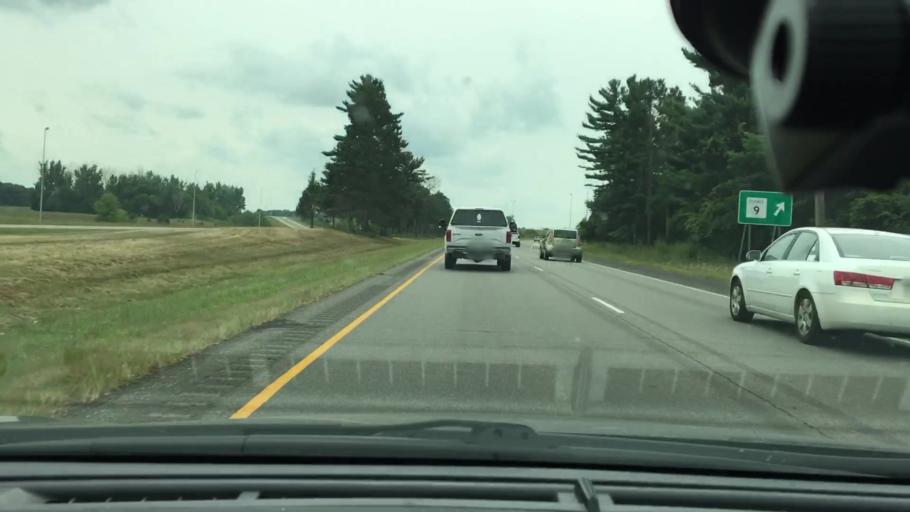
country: US
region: Minnesota
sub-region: Mille Lacs County
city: Princeton
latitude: 45.5066
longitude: -93.5830
